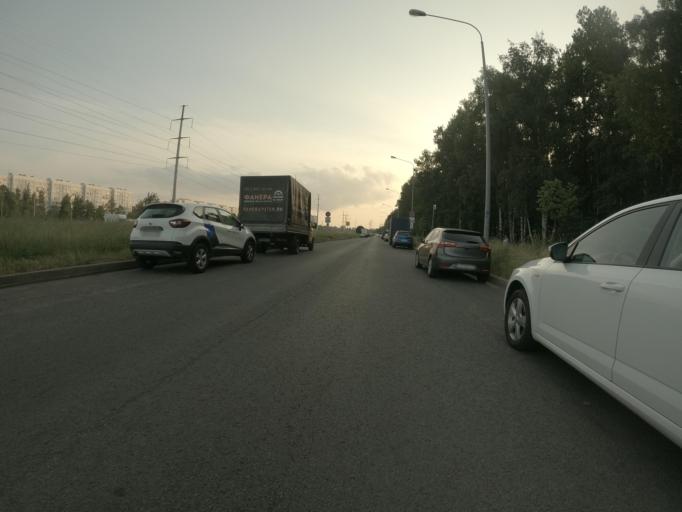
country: RU
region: St.-Petersburg
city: Krasnogvargeisky
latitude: 59.9756
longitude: 30.4309
